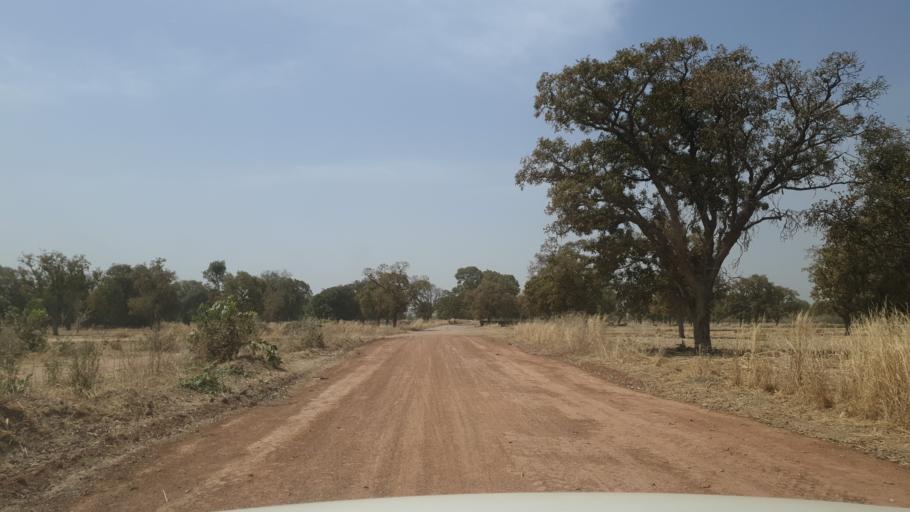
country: ML
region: Koulikoro
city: Kolokani
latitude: 13.4765
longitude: -8.1849
